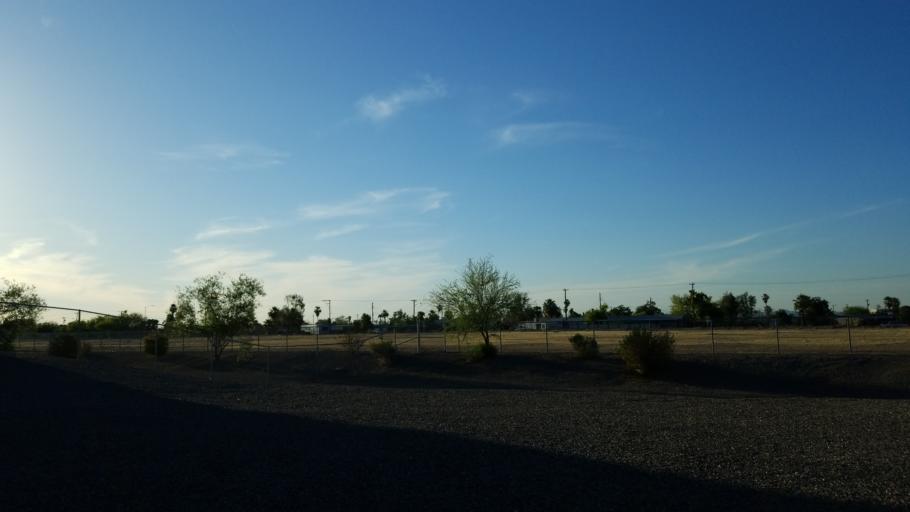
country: US
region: Arizona
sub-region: Maricopa County
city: Guadalupe
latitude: 33.3848
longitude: -112.0323
